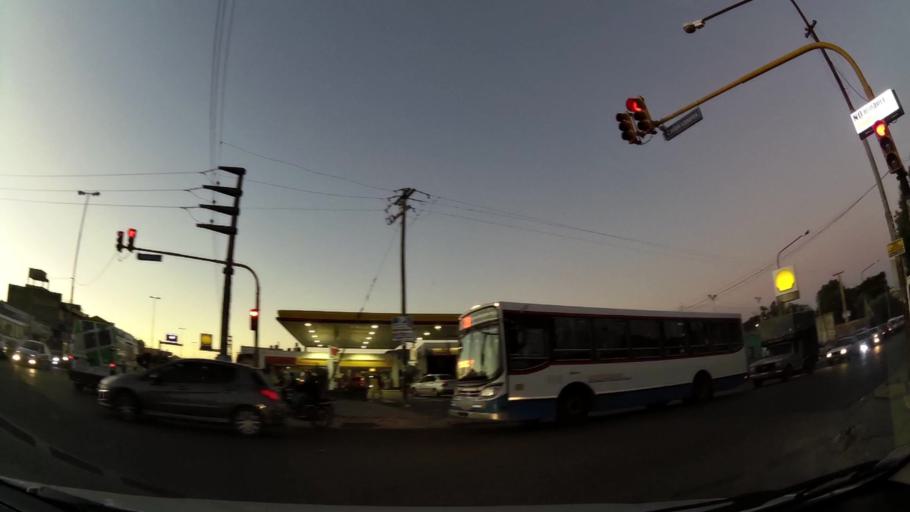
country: AR
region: Buenos Aires
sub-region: Partido de Moron
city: Moron
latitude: -34.7049
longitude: -58.6161
